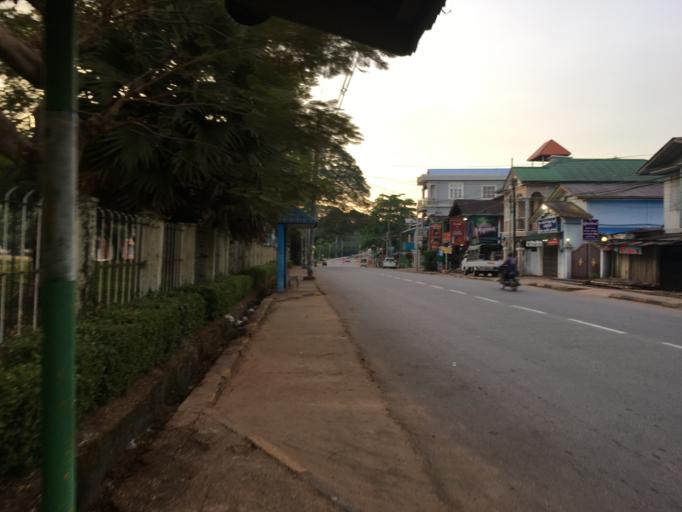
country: MM
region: Mon
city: Mawlamyine
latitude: 16.4662
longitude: 97.6272
